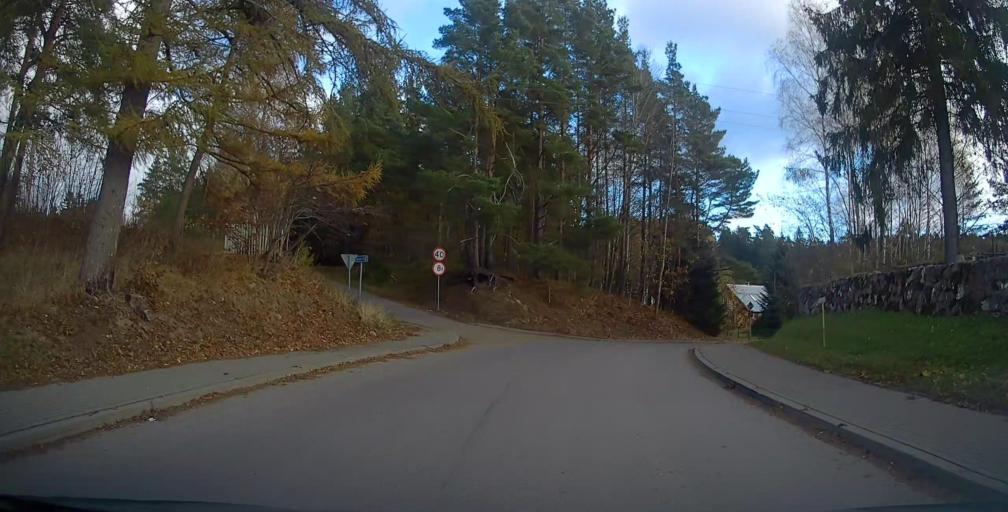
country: PL
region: Podlasie
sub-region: Suwalki
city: Suwalki
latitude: 54.2875
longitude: 22.8845
